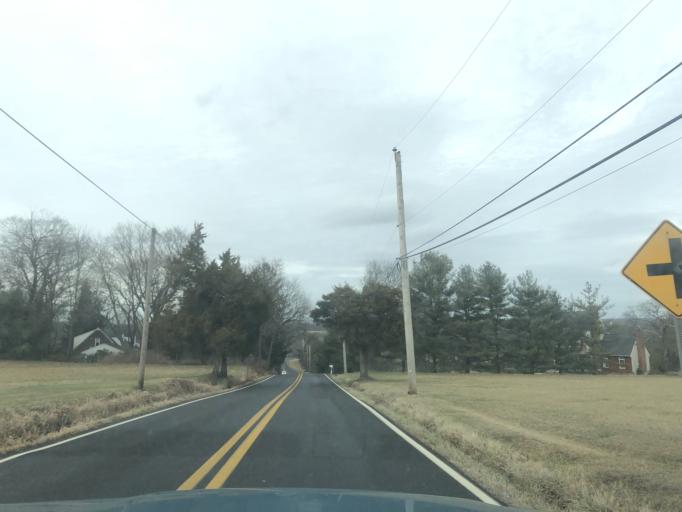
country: US
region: Pennsylvania
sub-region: Montgomery County
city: Harleysville
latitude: 40.2631
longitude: -75.4088
